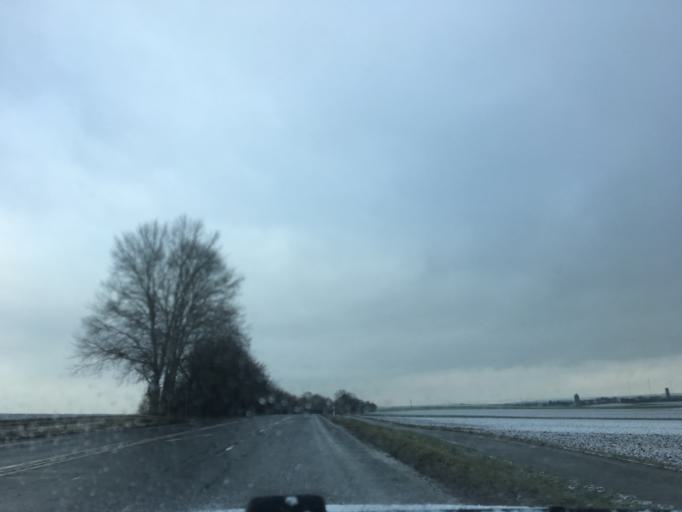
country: DE
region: Rheinland-Pfalz
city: Morschheim
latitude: 49.6901
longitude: 8.0142
